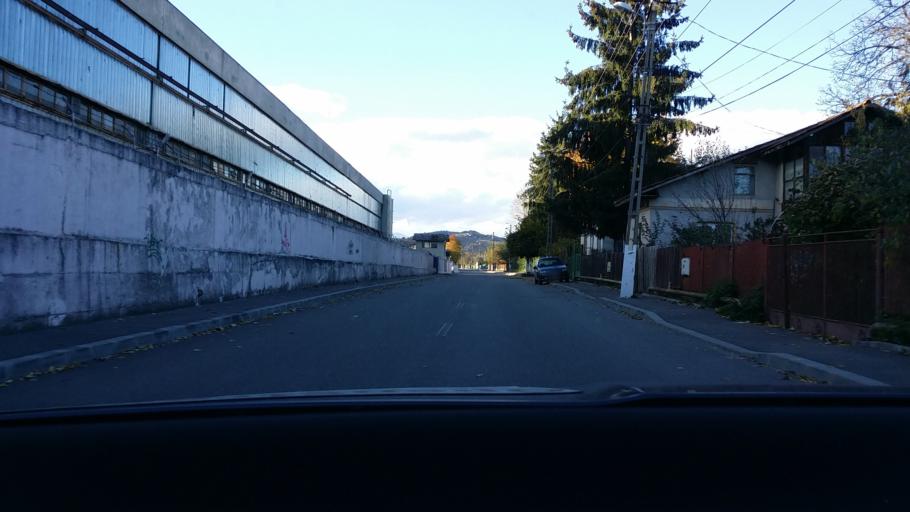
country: RO
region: Prahova
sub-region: Municipiul Campina
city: Campina
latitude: 45.1353
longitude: 25.7423
